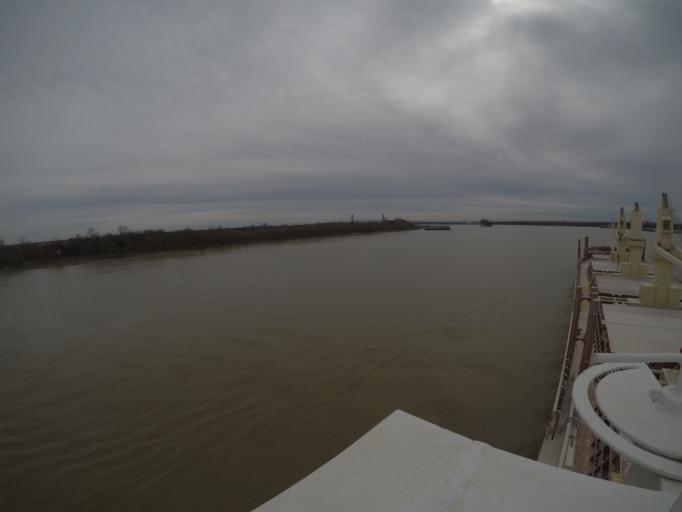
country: US
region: Louisiana
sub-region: Saint Charles Parish
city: New Sarpy
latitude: 29.9644
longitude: -90.3954
